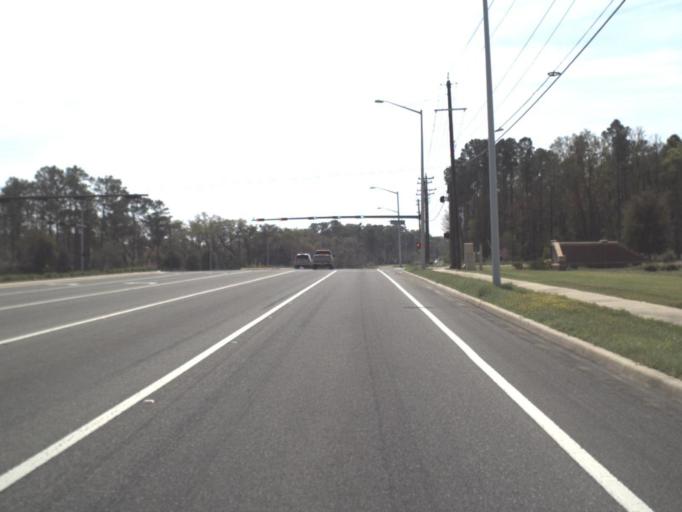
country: US
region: Florida
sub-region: Leon County
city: Tallahassee
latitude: 30.3881
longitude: -84.2357
